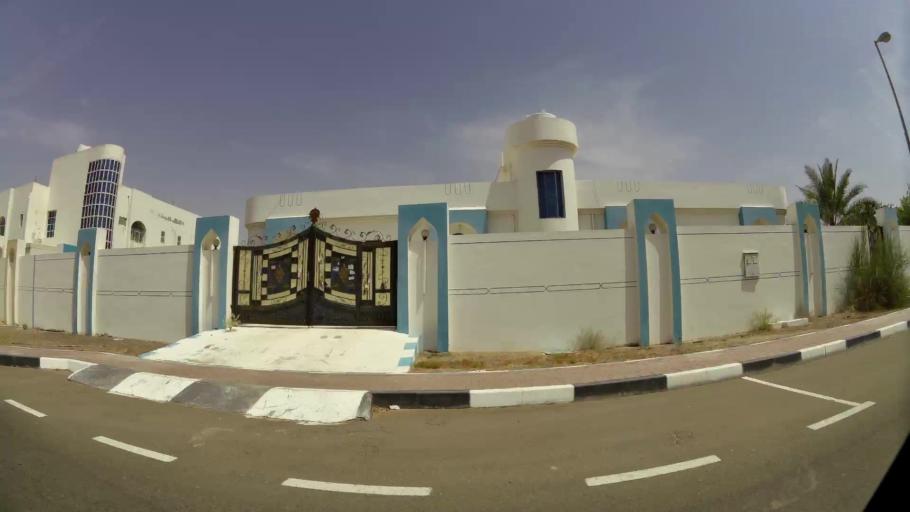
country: AE
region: Abu Dhabi
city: Al Ain
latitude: 24.1768
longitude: 55.7167
